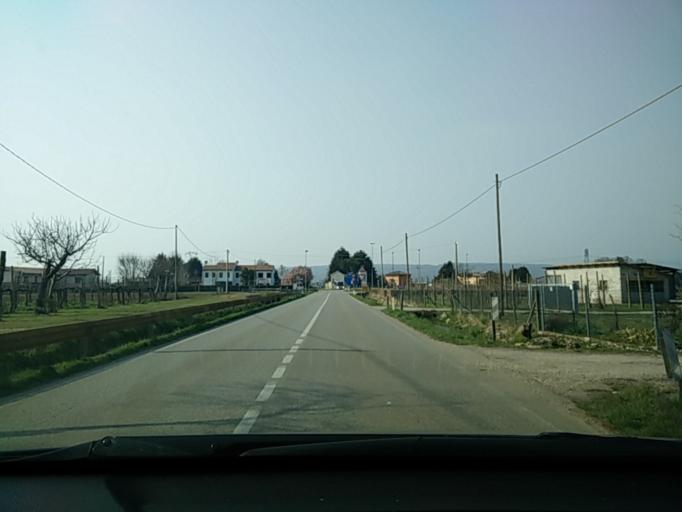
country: IT
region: Veneto
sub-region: Provincia di Treviso
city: Camalo
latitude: 45.7615
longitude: 12.1586
